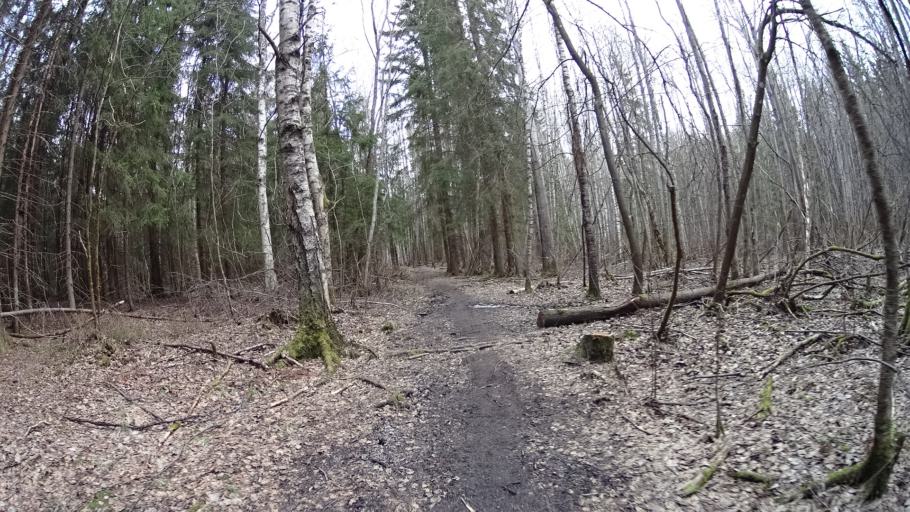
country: FI
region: Uusimaa
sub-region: Helsinki
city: Kilo
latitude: 60.2448
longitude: 24.7892
